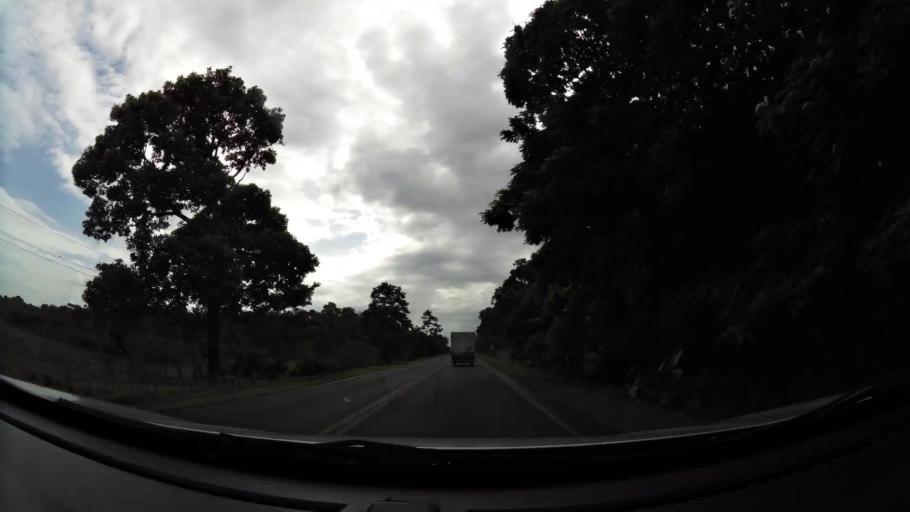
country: CR
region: Limon
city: Pocora
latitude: 10.1783
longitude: -83.6196
